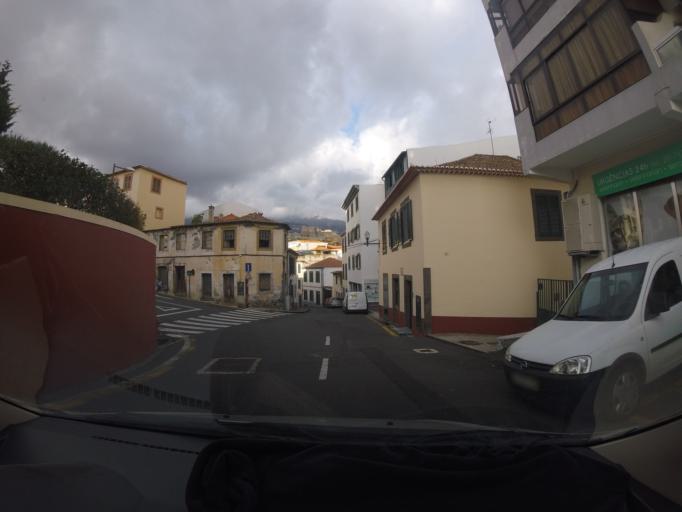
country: PT
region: Madeira
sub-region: Funchal
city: Funchal
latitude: 32.6475
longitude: -16.9183
